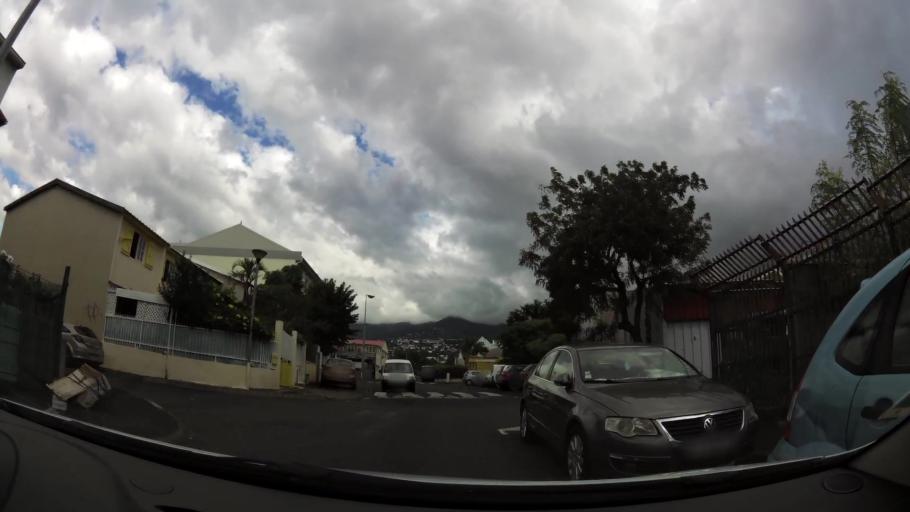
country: RE
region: Reunion
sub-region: Reunion
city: Saint-Denis
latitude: -20.8930
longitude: 55.4772
